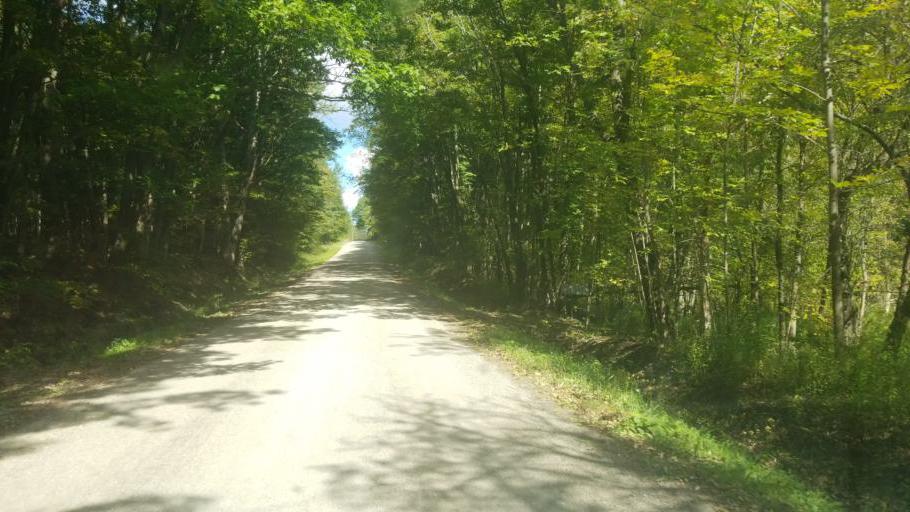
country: US
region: New York
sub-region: Allegany County
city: Cuba
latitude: 42.1961
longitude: -78.3089
